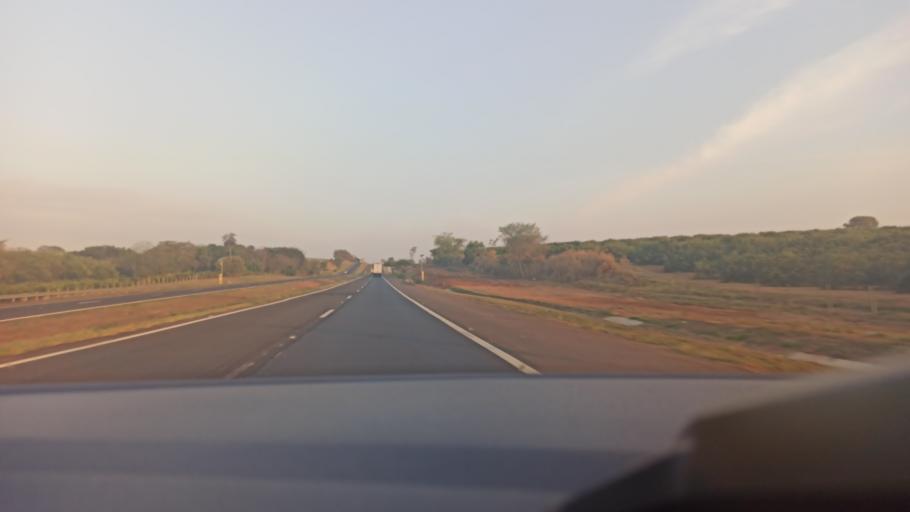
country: BR
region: Sao Paulo
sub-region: Santa Adelia
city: Santa Adelia
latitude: -21.3969
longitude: -48.7123
